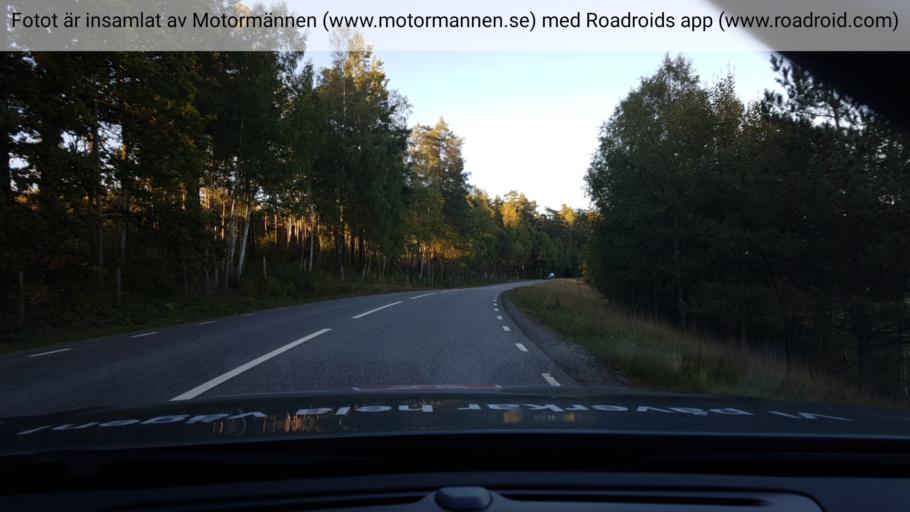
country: SE
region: Stockholm
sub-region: Haninge Kommun
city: Jordbro
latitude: 59.1877
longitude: 18.1013
